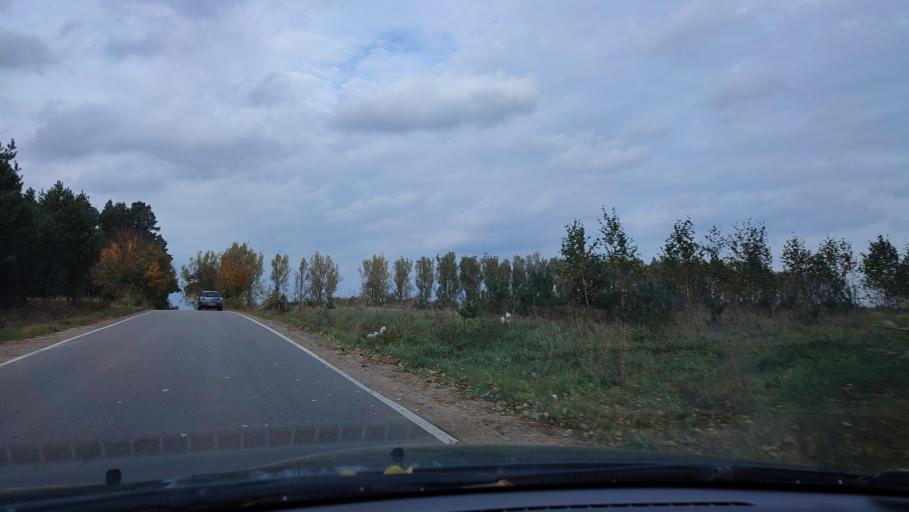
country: PL
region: Masovian Voivodeship
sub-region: Powiat mlawski
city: Mlawa
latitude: 53.1833
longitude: 20.3765
